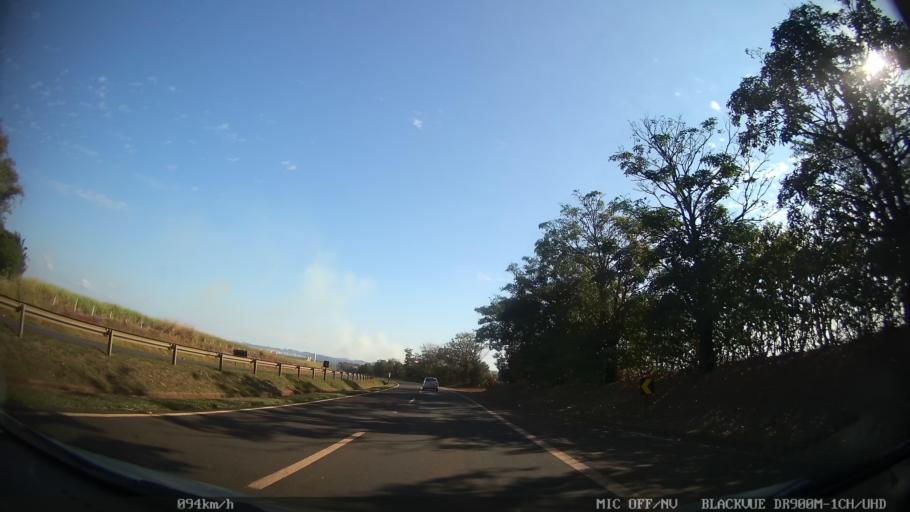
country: BR
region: Sao Paulo
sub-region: Iracemapolis
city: Iracemapolis
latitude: -22.6700
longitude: -47.5535
